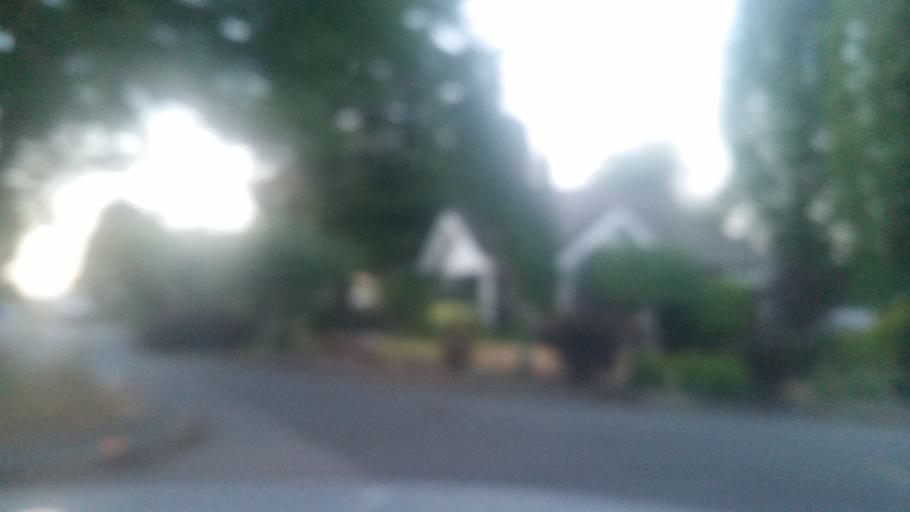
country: US
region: Washington
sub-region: King County
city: Shoreline
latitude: 47.6942
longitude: -122.3633
